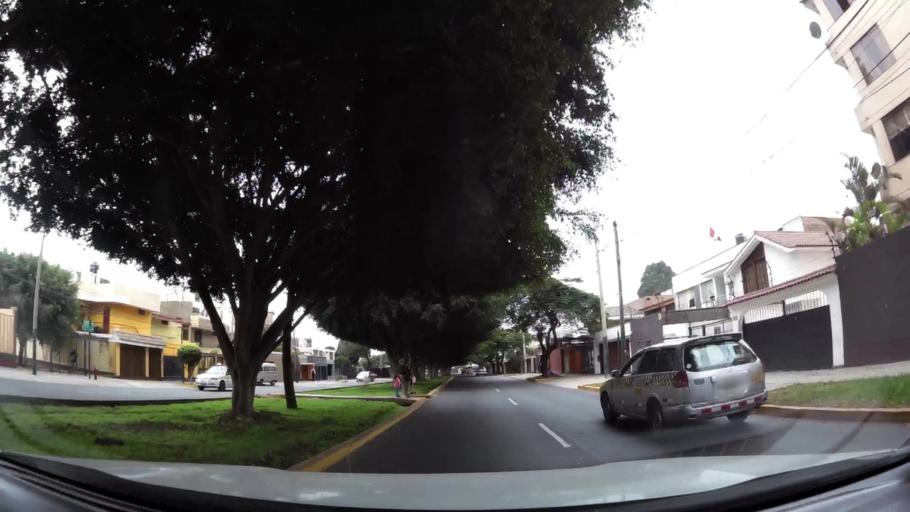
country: PE
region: Lima
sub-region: Lima
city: Surco
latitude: -12.1340
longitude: -77.0121
